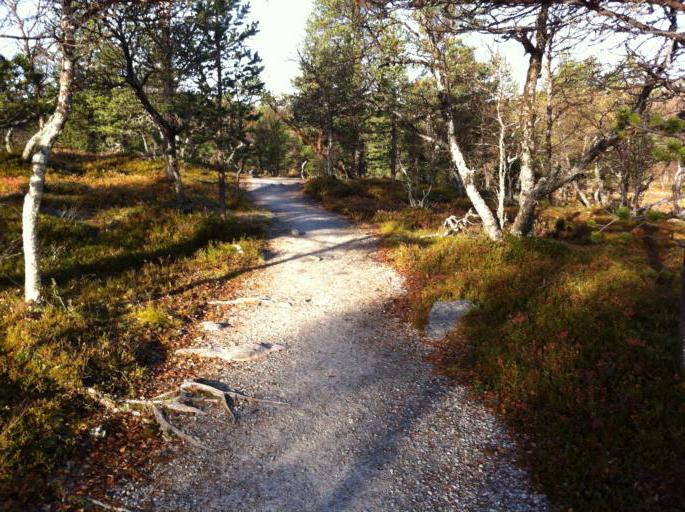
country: NO
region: Hedmark
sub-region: Engerdal
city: Engerdal
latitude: 62.1063
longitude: 12.2893
